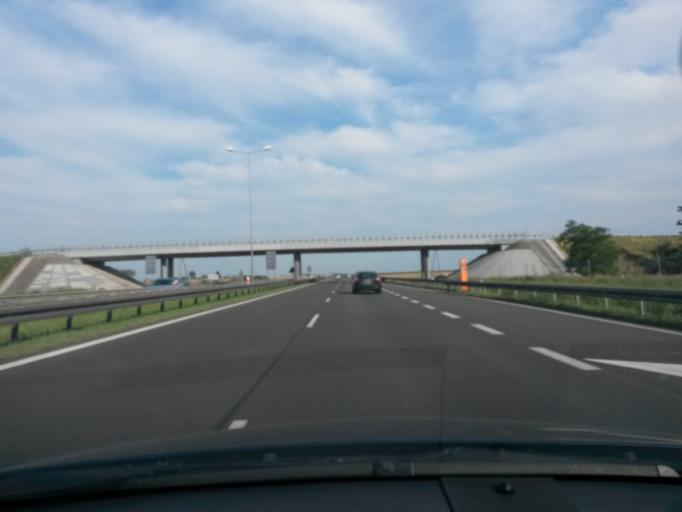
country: PL
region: Greater Poland Voivodeship
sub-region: Powiat slupecki
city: Ladek
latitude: 52.2201
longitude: 17.9570
